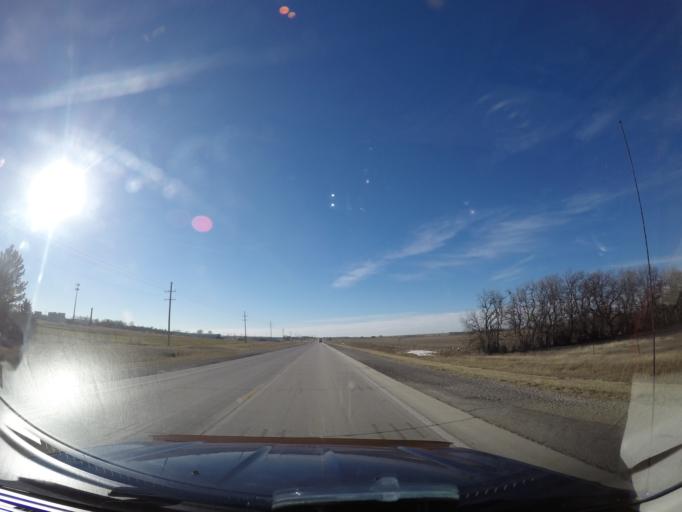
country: US
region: Kansas
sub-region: Marion County
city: Hillsboro
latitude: 38.3627
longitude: -97.2008
